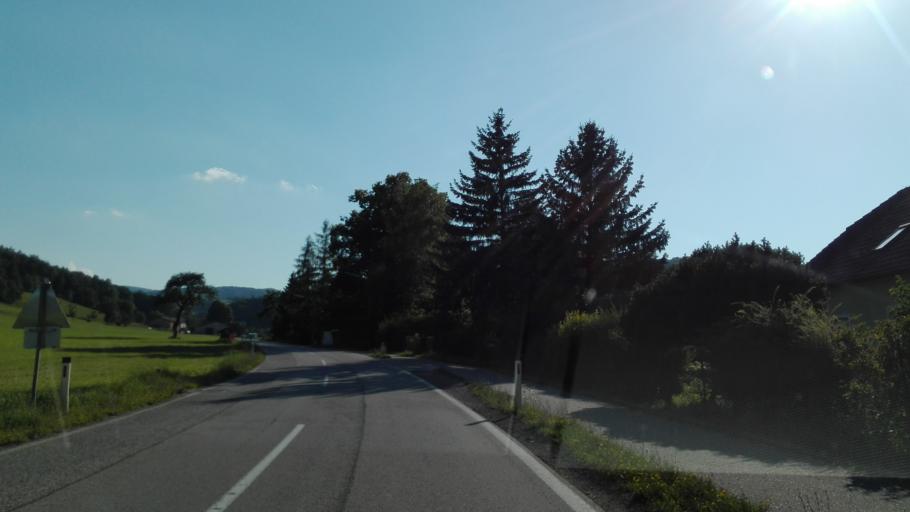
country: AT
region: Lower Austria
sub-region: Politischer Bezirk Sankt Polten
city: Altlengbach
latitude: 48.1207
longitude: 15.8914
